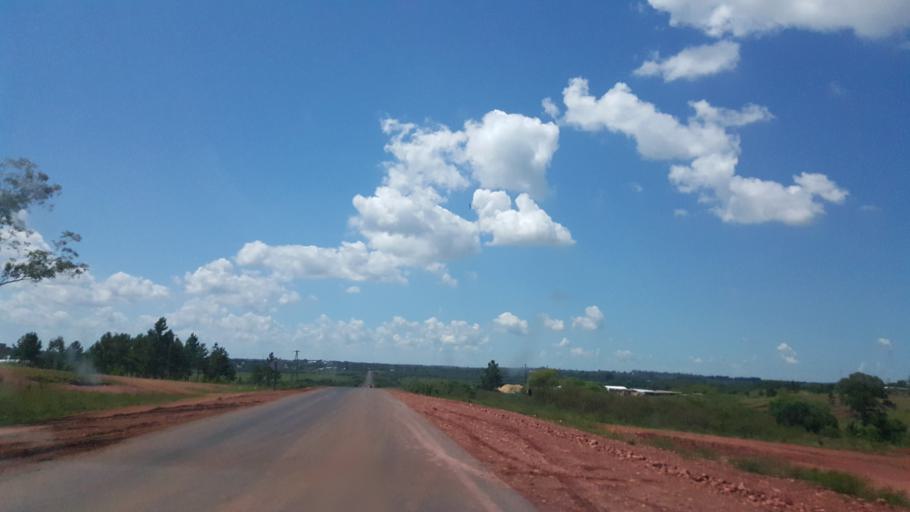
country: AR
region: Corrientes
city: Santo Tome
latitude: -28.5199
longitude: -56.0570
